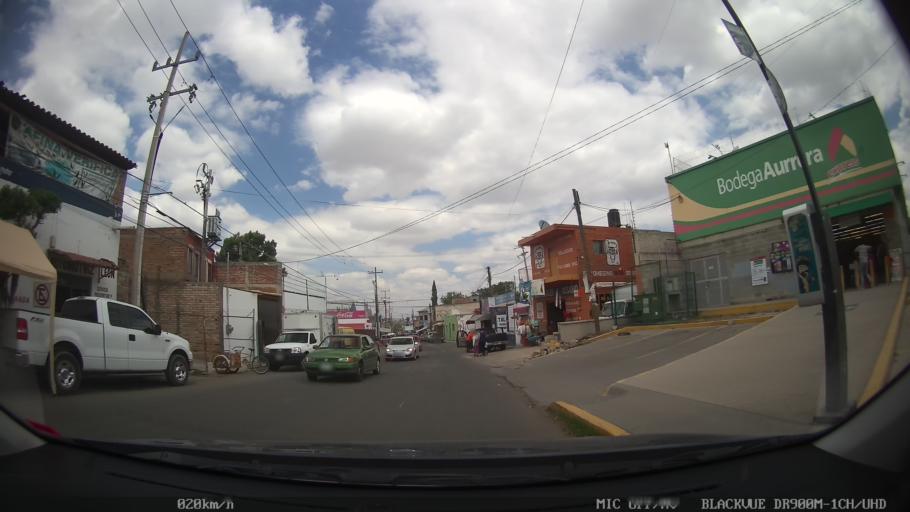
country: MX
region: Jalisco
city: Tonala
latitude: 20.6418
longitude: -103.2595
